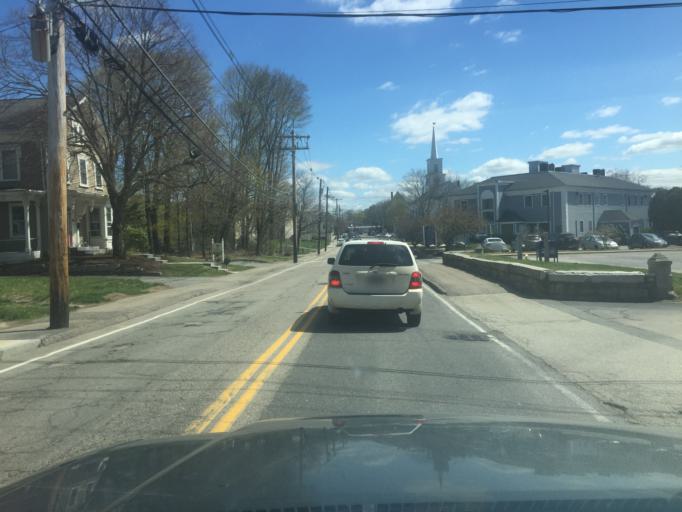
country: US
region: Massachusetts
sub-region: Norfolk County
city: Medfield
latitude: 42.1887
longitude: -71.3075
